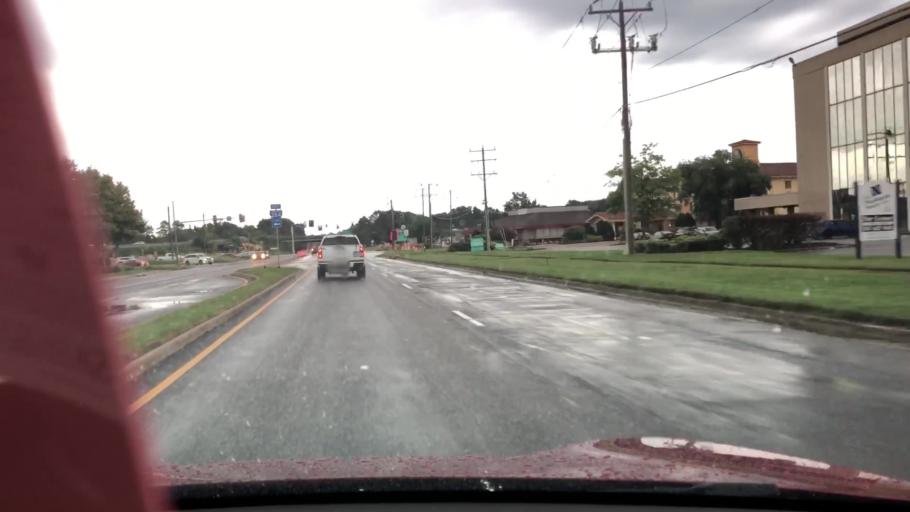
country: US
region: Virginia
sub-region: City of Chesapeake
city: Chesapeake
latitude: 36.8430
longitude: -76.1857
